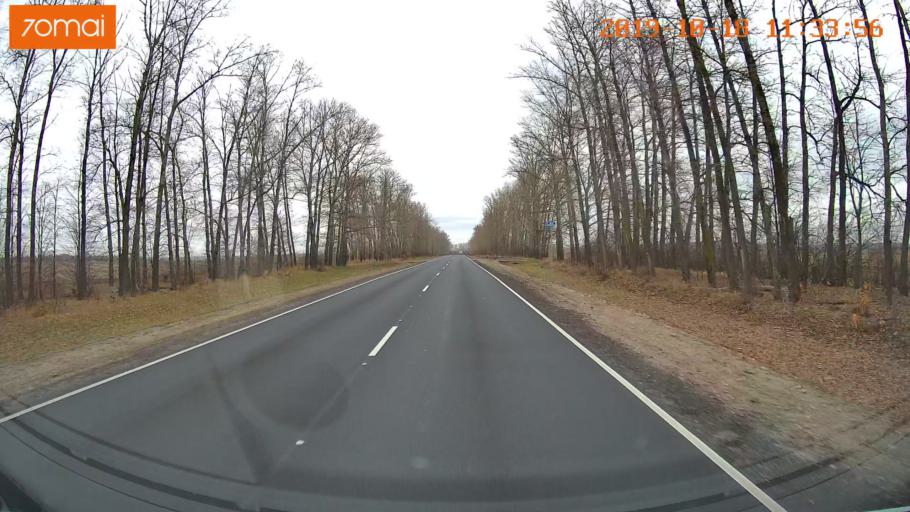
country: RU
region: Rjazan
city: Oktyabr'skiy
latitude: 54.1376
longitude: 38.7525
